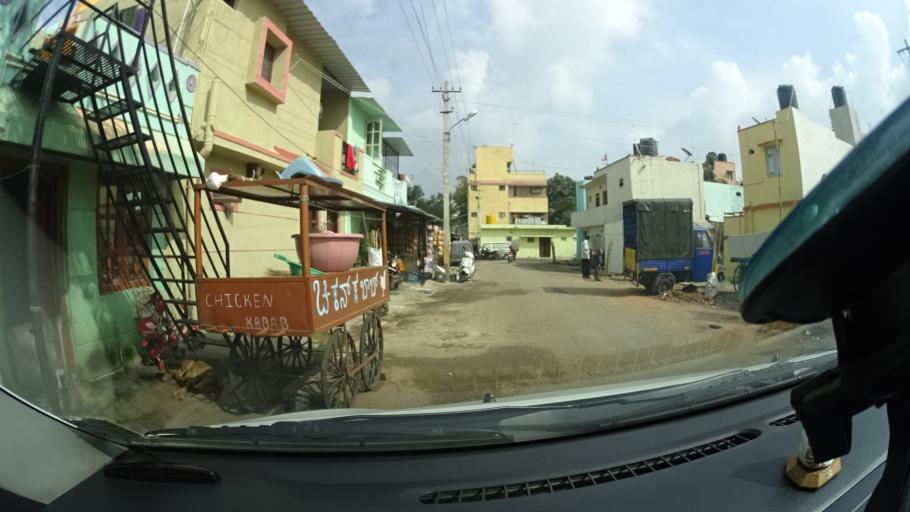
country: IN
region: Karnataka
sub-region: Bangalore Urban
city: Yelahanka
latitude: 13.0901
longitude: 77.5808
